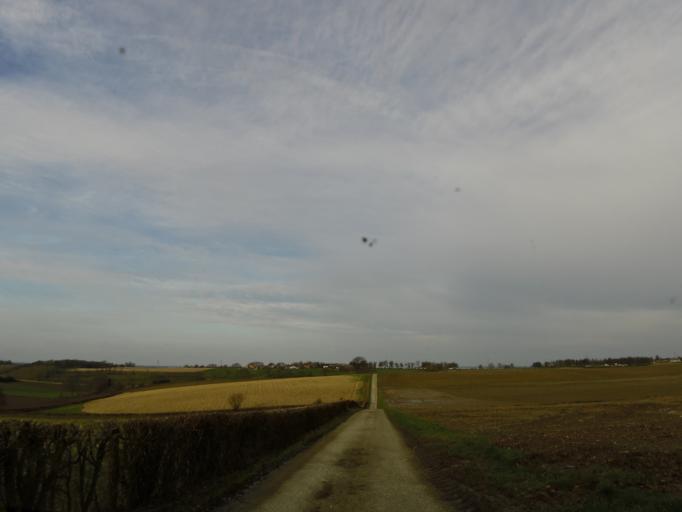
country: NL
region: Limburg
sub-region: Gemeente Voerendaal
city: Ubachsberg
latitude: 50.8423
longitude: 5.9396
